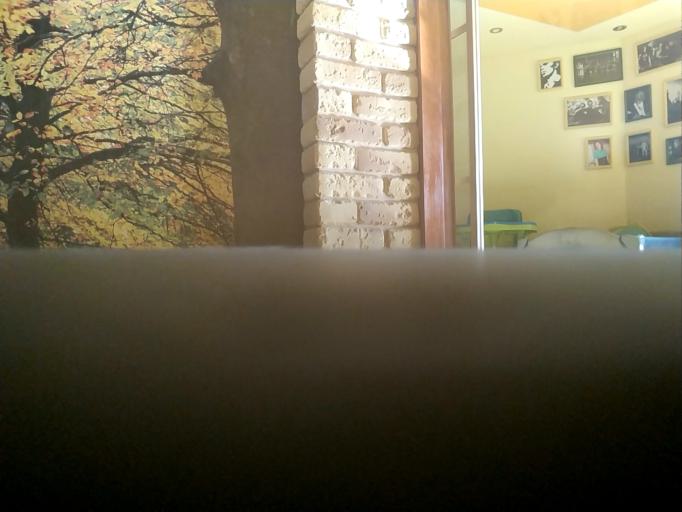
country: RU
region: Smolensk
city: Temkino
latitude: 54.9673
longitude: 34.9501
